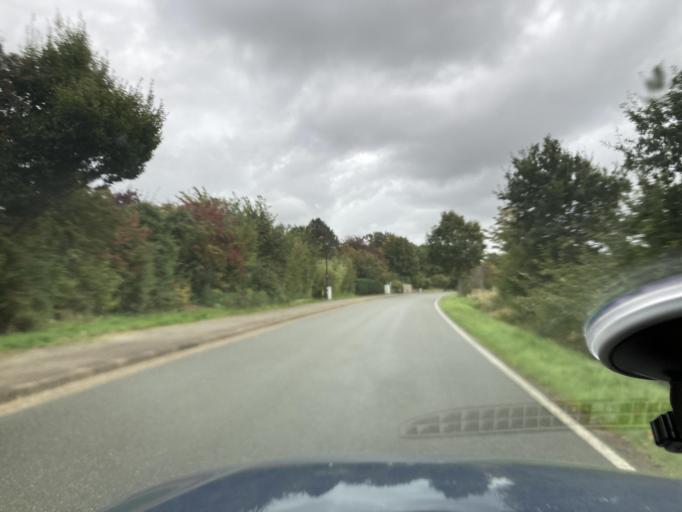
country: DE
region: Schleswig-Holstein
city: Lohe-Rickelshof
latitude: 54.2160
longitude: 9.0694
